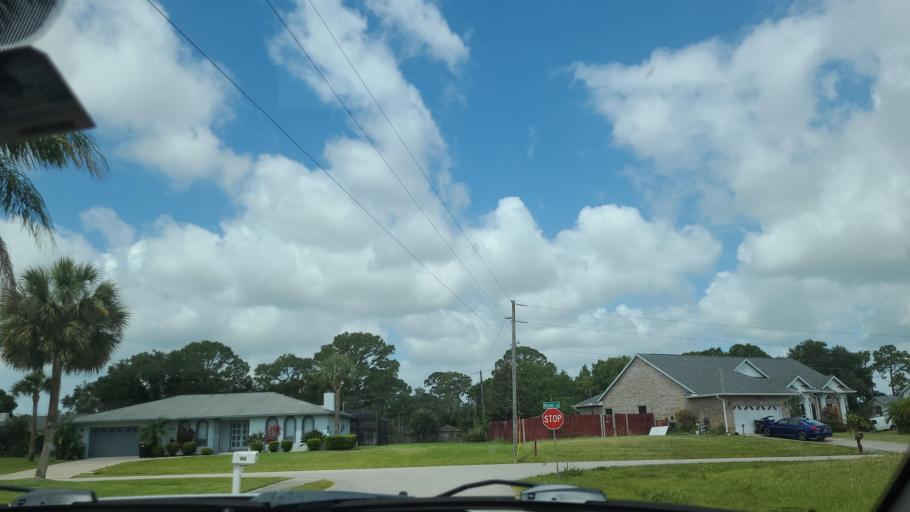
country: US
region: Florida
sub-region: Brevard County
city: West Melbourne
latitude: 28.0248
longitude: -80.6642
